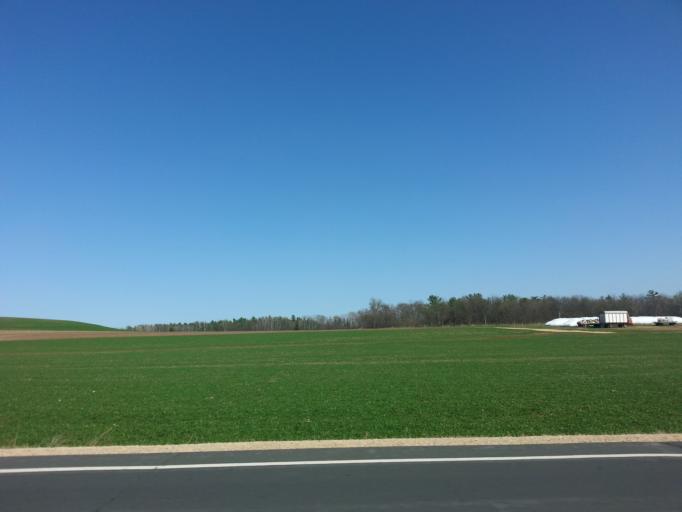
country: US
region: Wisconsin
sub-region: Pepin County
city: Durand
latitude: 44.6885
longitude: -91.9487
